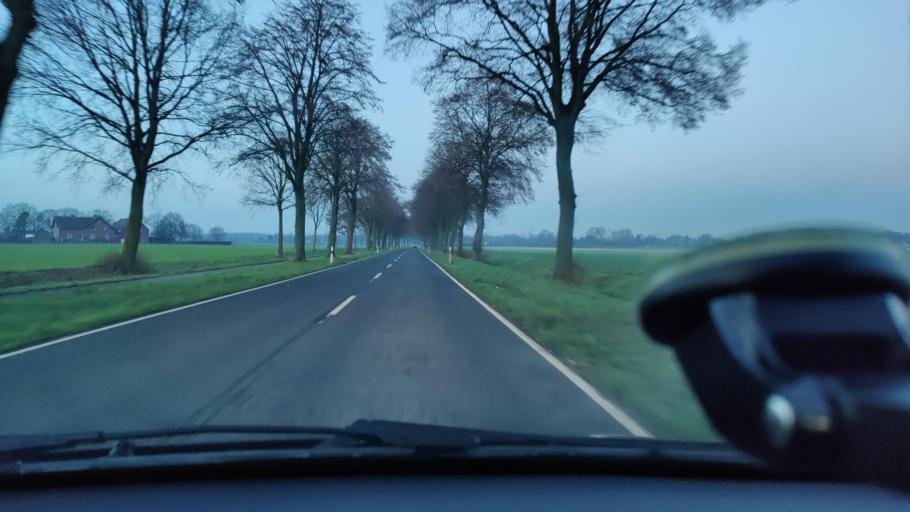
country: DE
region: North Rhine-Westphalia
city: Rheinberg
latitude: 51.6002
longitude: 6.6106
